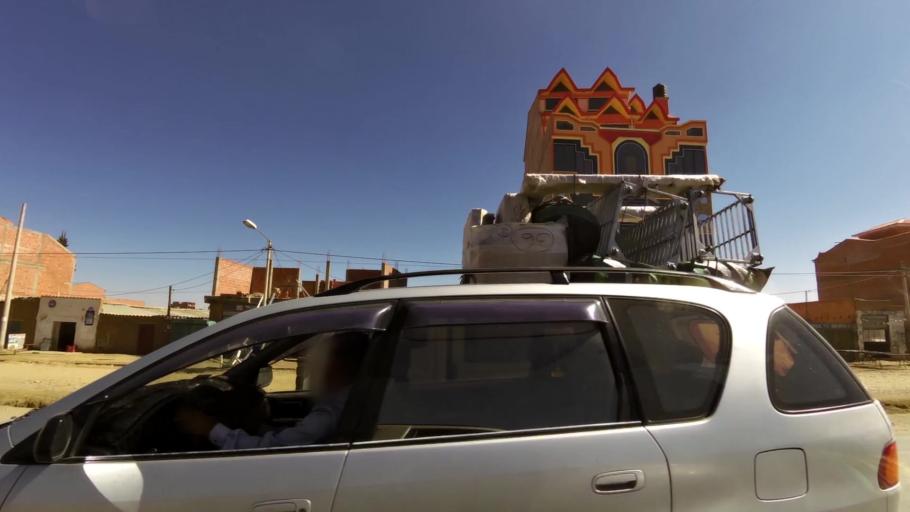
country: BO
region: La Paz
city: La Paz
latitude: -16.5634
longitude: -68.2175
